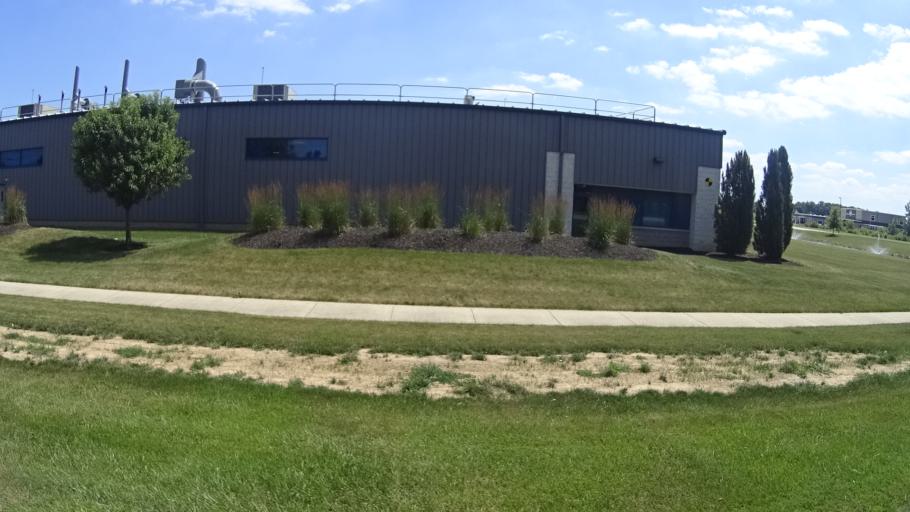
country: US
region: Ohio
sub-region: Erie County
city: Huron
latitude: 41.3979
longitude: -82.5911
